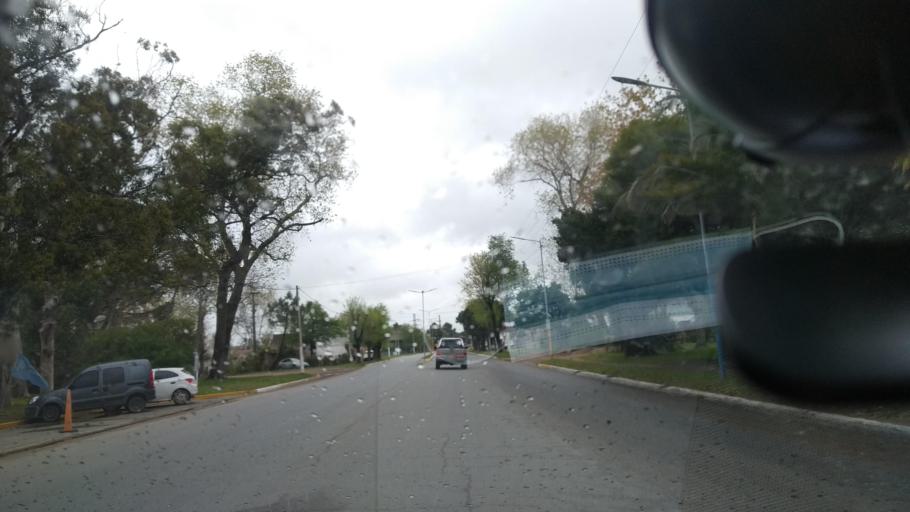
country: AR
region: Buenos Aires
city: San Clemente del Tuyu
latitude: -36.3788
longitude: -56.7206
